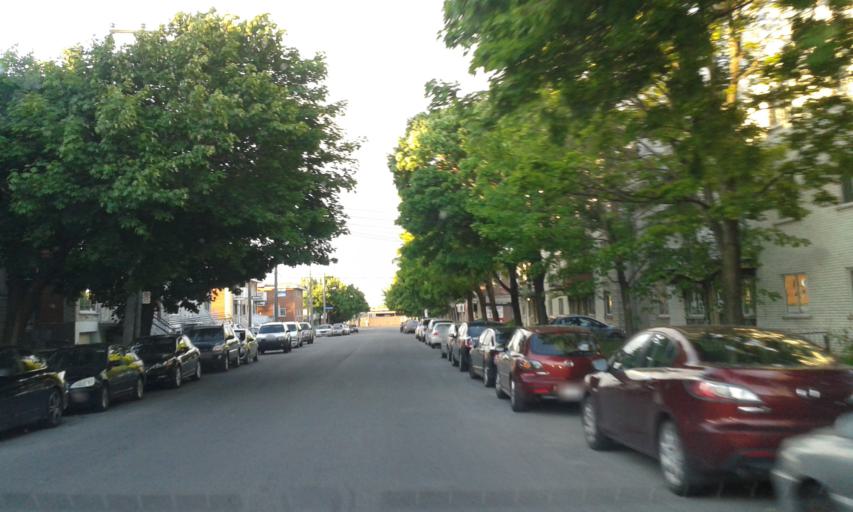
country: CA
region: Quebec
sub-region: Montreal
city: Saint-Leonard
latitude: 45.5858
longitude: -73.6315
